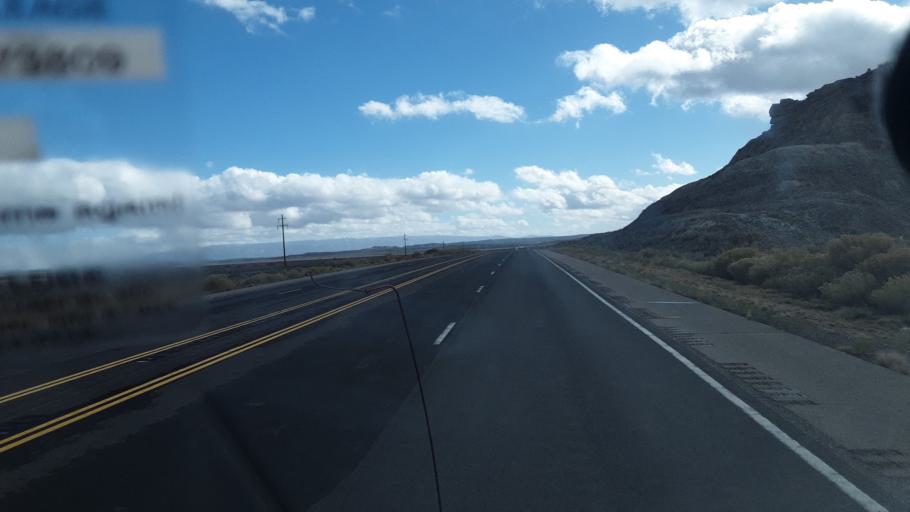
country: US
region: New Mexico
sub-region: Rio Arriba County
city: Santa Teresa
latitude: 36.1413
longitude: -107.2469
